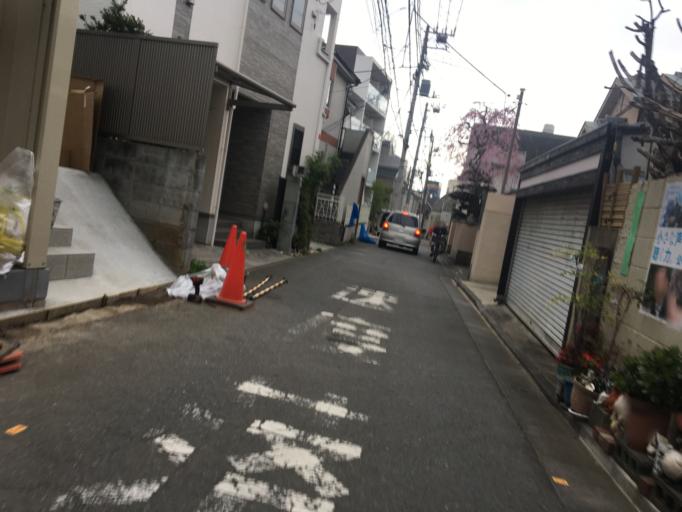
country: JP
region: Tokyo
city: Tokyo
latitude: 35.7082
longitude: 139.6712
